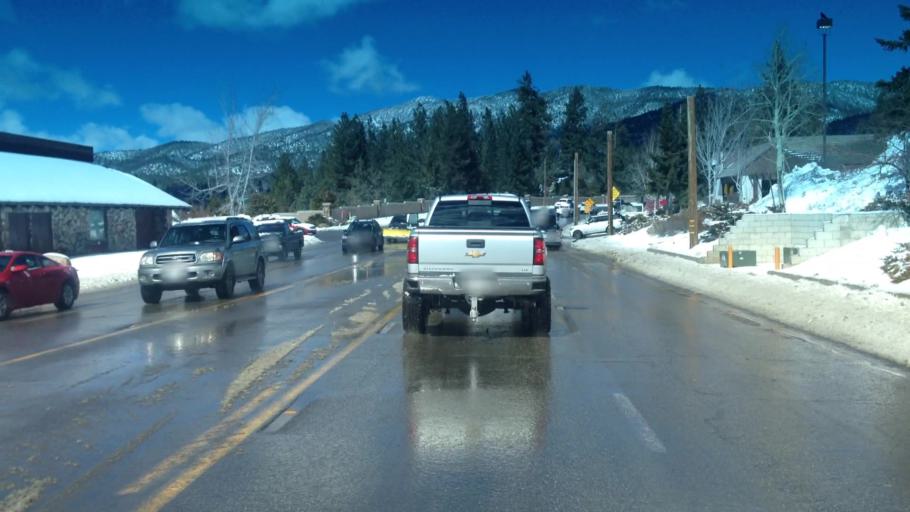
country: US
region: California
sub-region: San Bernardino County
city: Big Bear Lake
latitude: 34.2527
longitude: -116.8845
